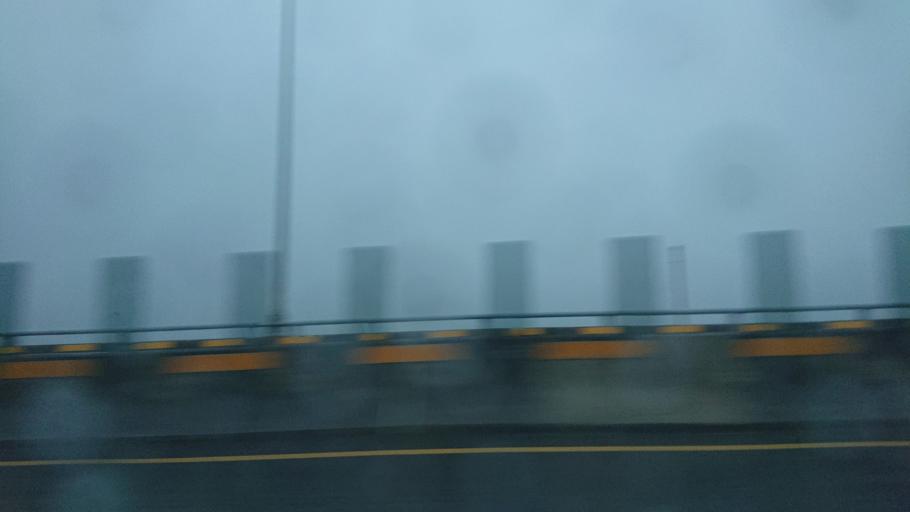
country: TW
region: Taiwan
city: Fengyuan
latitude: 24.3190
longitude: 120.5655
